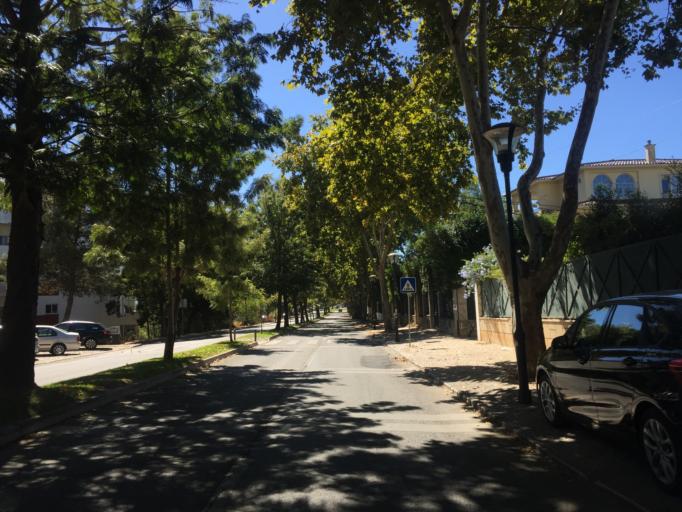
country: PT
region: Lisbon
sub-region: Cascais
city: Cascais
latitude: 38.6999
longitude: -9.4329
